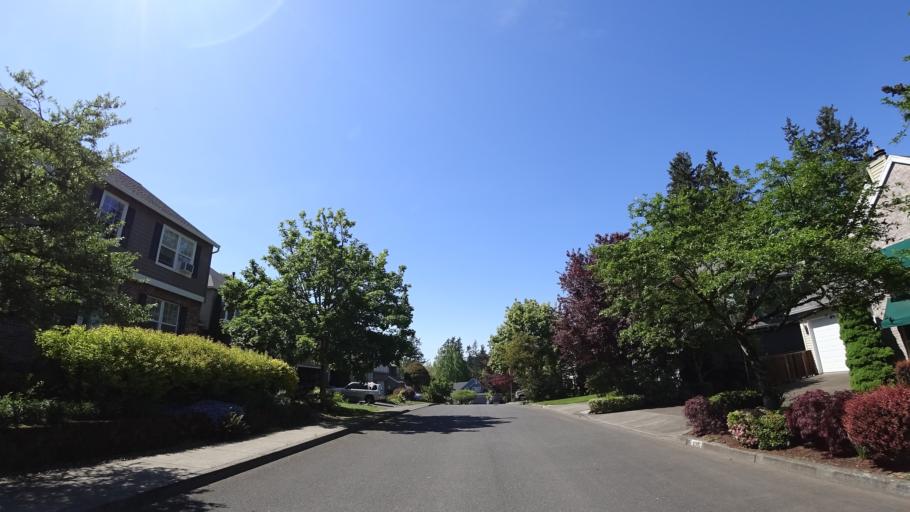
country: US
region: Oregon
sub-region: Washington County
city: Raleigh Hills
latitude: 45.4834
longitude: -122.7419
